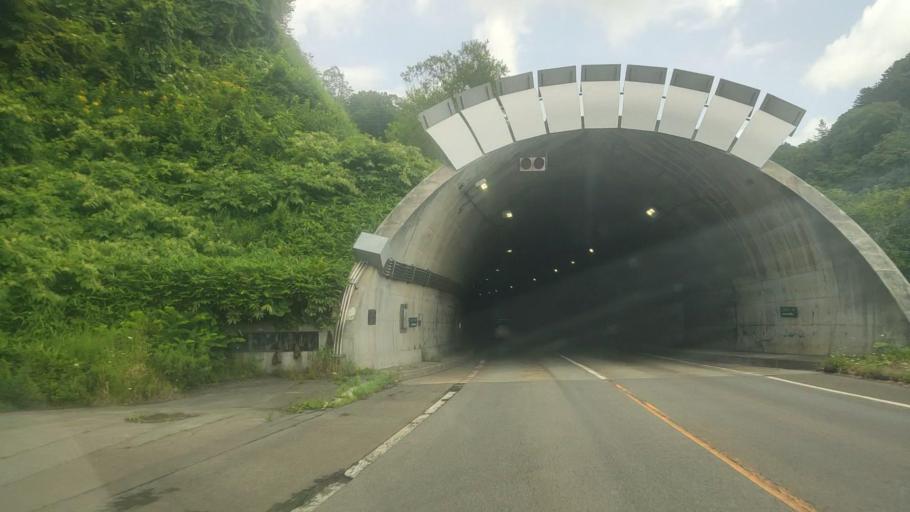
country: JP
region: Hokkaido
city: Niseko Town
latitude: 42.5948
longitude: 140.5413
